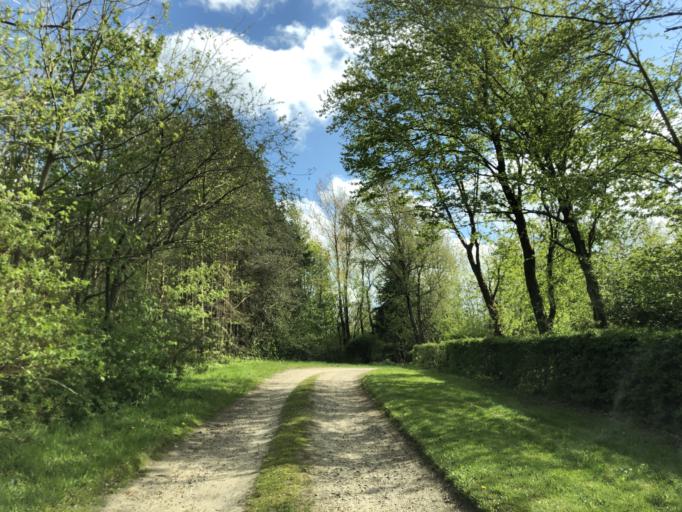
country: DK
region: Central Jutland
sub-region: Herning Kommune
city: Avlum
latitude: 56.3017
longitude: 8.7644
